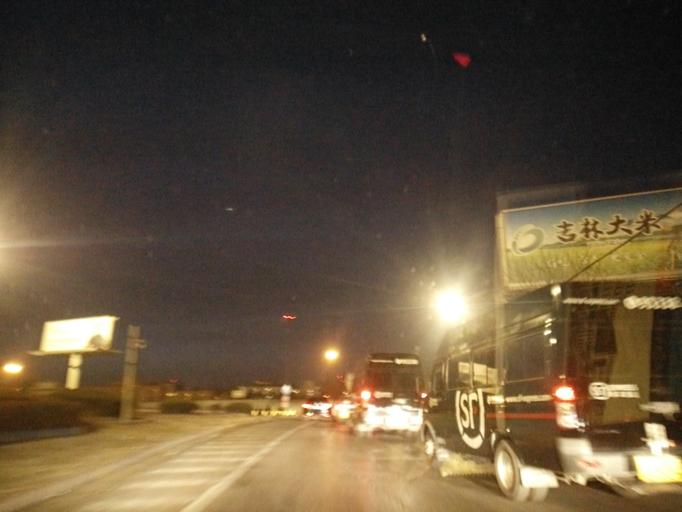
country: CN
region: Beijing
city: Tianzhu
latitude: 40.0764
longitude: 116.5821
